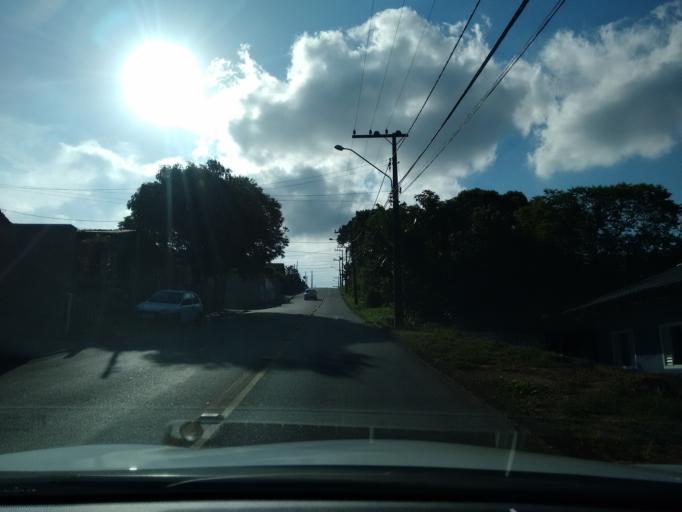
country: BR
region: Santa Catarina
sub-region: Blumenau
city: Blumenau
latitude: -26.8700
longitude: -49.0742
